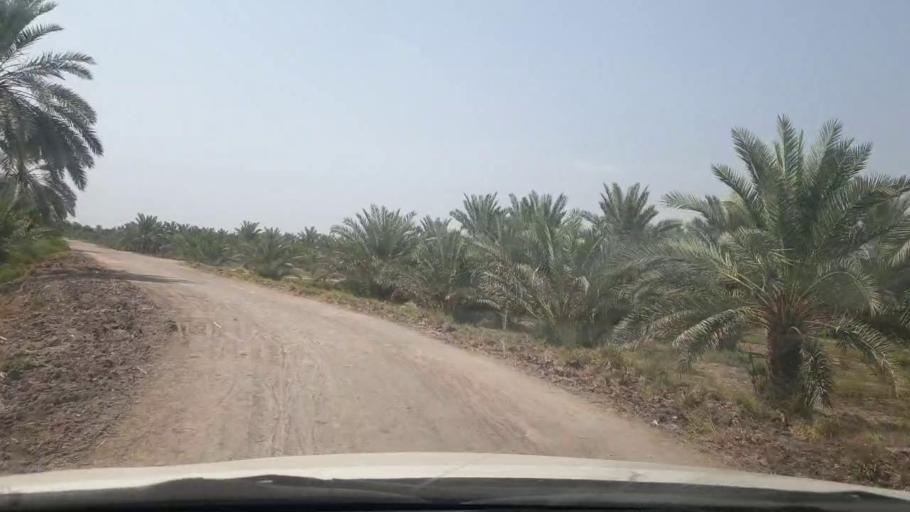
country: PK
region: Sindh
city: Khairpur
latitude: 27.5589
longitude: 68.8512
